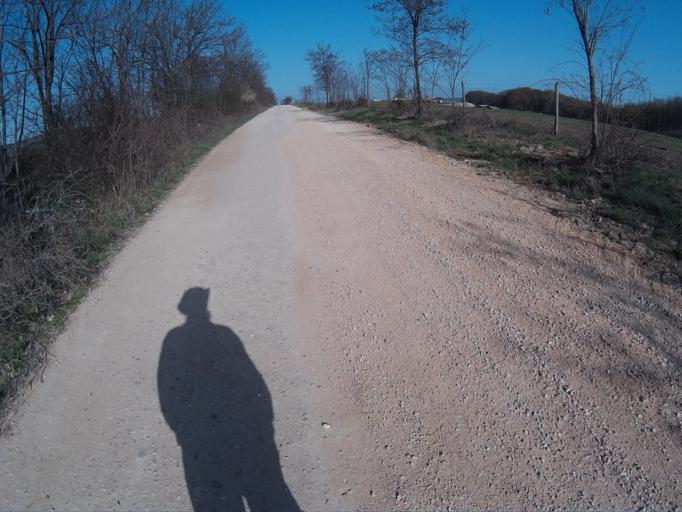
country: HU
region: Veszprem
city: Herend
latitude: 47.1914
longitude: 17.8013
